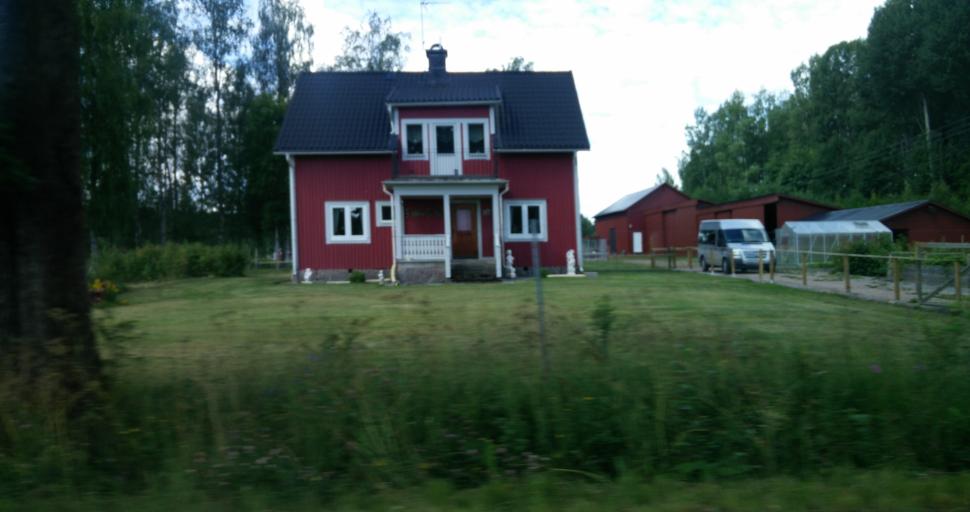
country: SE
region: Vaermland
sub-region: Hagfors Kommun
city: Ekshaerad
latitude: 60.1318
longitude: 13.4580
